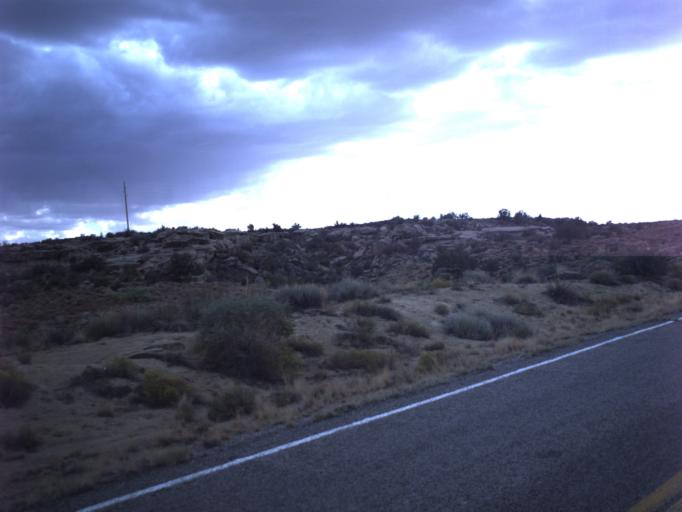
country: US
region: Utah
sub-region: San Juan County
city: Blanding
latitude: 37.4182
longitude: -109.4501
